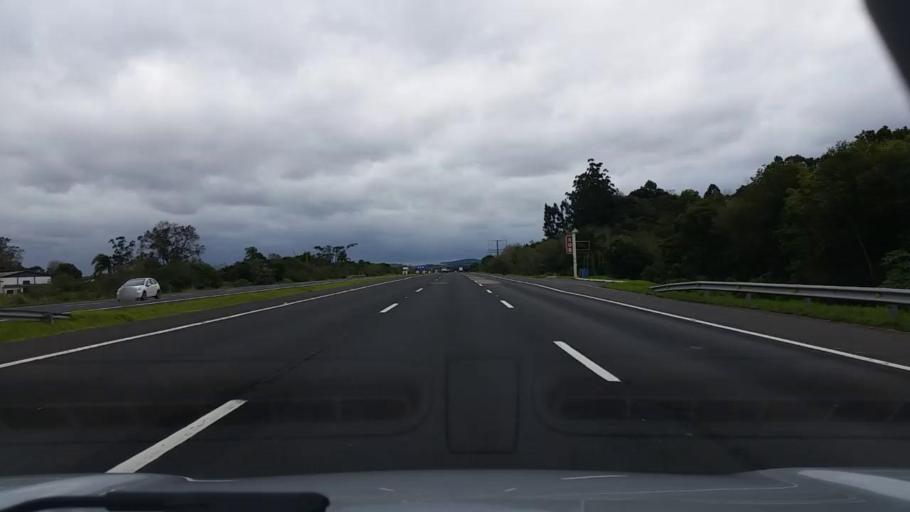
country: BR
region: Rio Grande do Sul
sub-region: Osorio
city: Osorio
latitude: -29.8760
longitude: -50.4261
